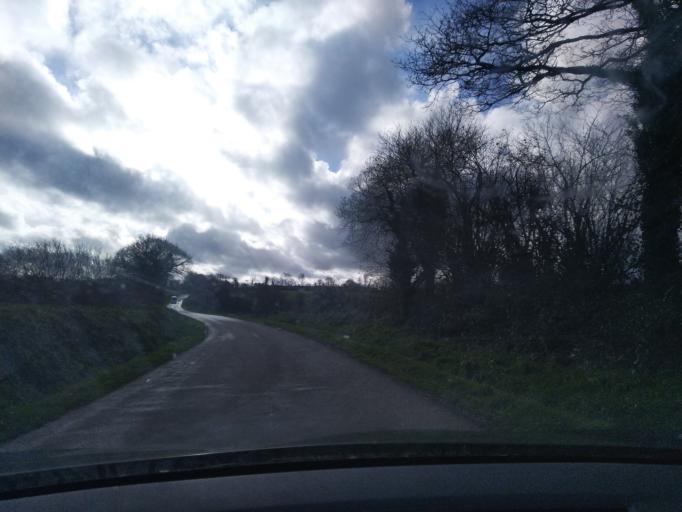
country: FR
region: Brittany
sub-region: Departement du Finistere
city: Guerlesquin
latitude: 48.4549
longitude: -3.5819
